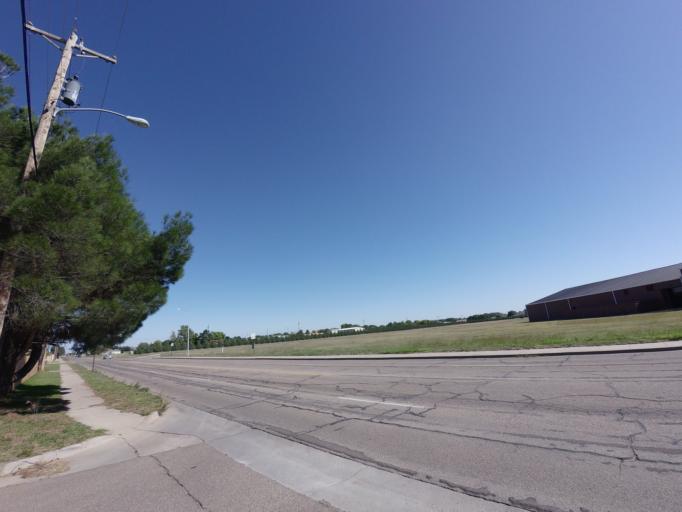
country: US
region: New Mexico
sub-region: Curry County
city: Clovis
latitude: 34.4253
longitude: -103.1787
